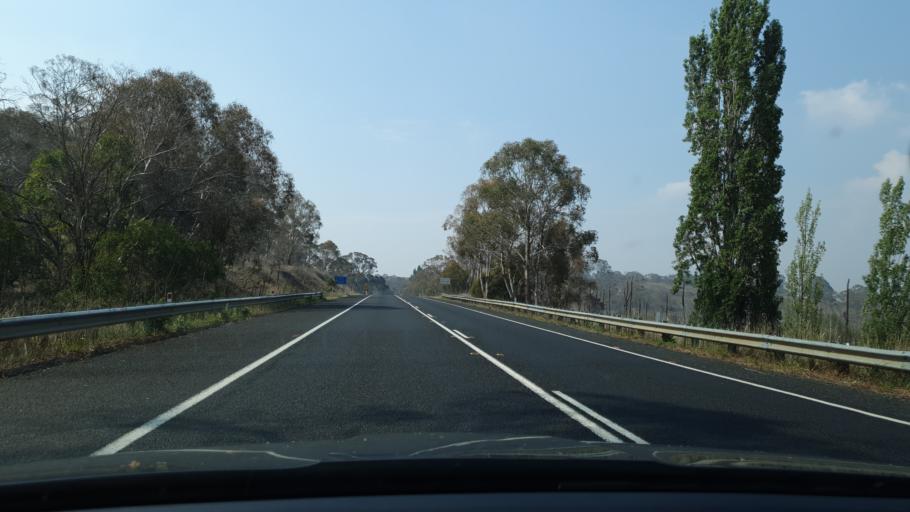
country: AU
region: New South Wales
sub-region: Guyra
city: Guyra
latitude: -29.9826
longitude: 151.7159
